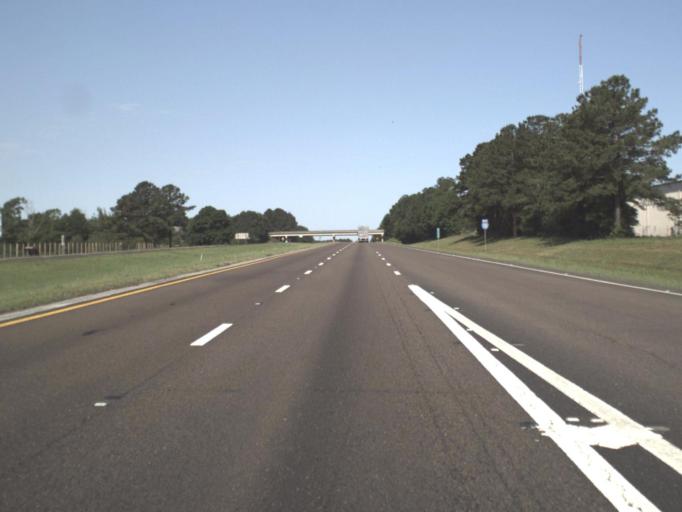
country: US
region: Florida
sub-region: Holmes County
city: Bonifay
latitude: 30.7631
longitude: -85.6903
